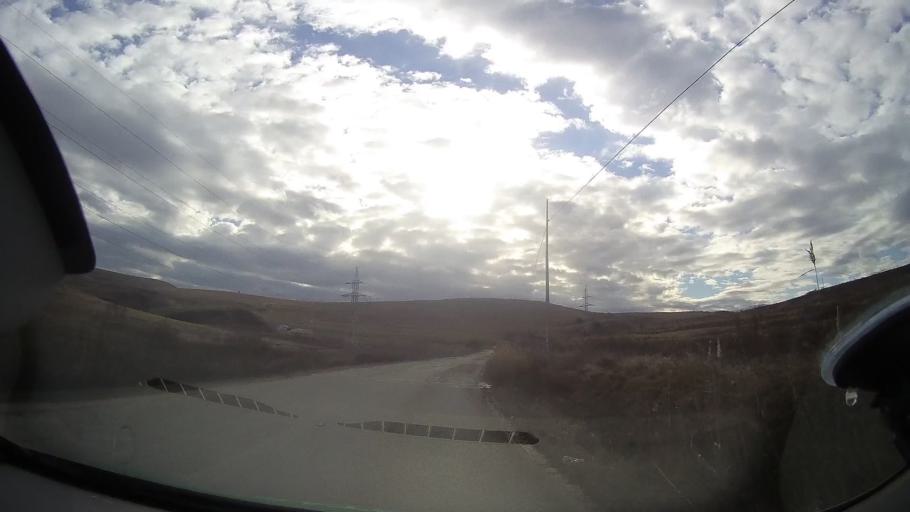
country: RO
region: Cluj
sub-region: Comuna Baisoara
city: Baisoara
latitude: 46.5982
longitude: 23.4640
